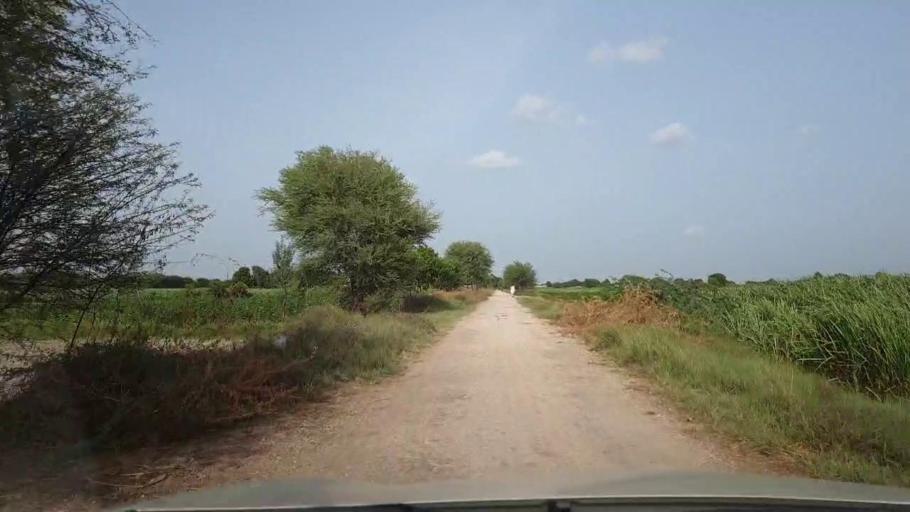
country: PK
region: Sindh
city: Tando Ghulam Ali
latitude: 25.1470
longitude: 68.9643
